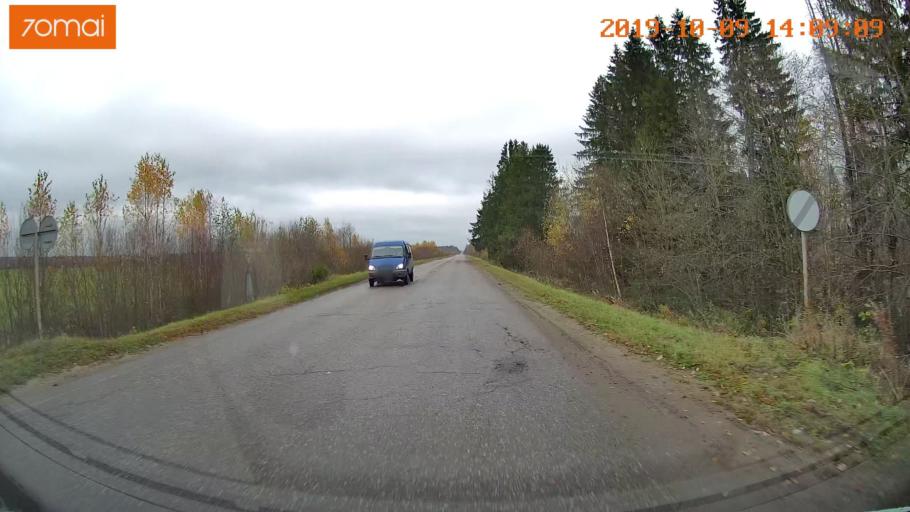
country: RU
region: Kostroma
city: Buy
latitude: 58.4802
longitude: 41.4463
